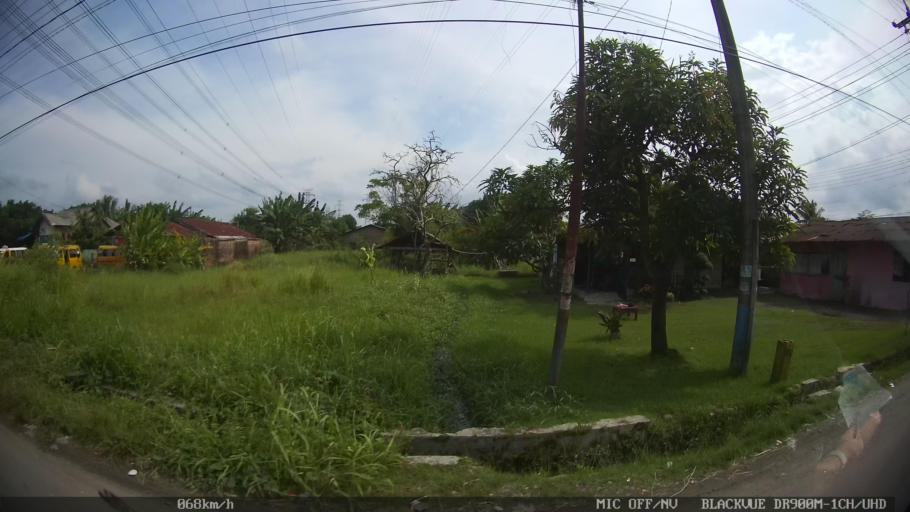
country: ID
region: North Sumatra
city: Percut
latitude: 3.6070
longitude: 98.7885
